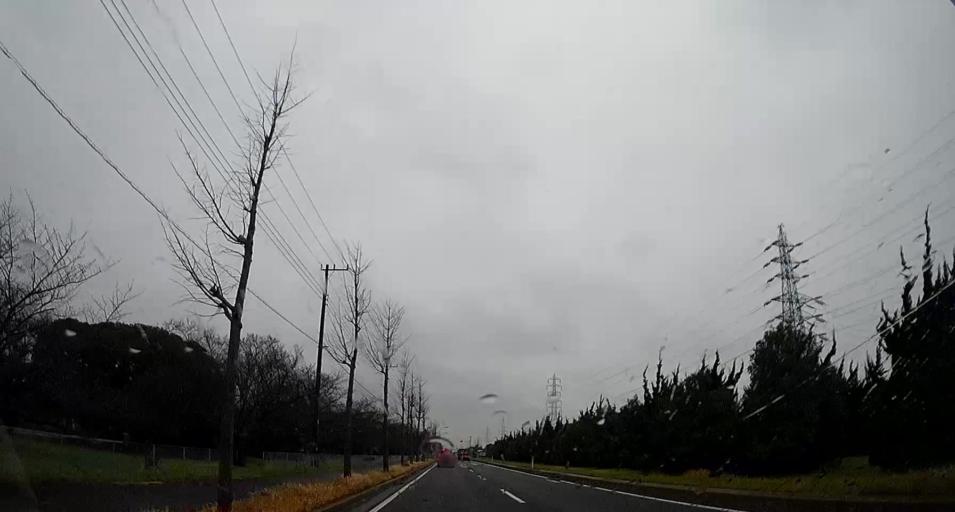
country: JP
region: Chiba
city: Ichihara
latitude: 35.5039
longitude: 140.0514
